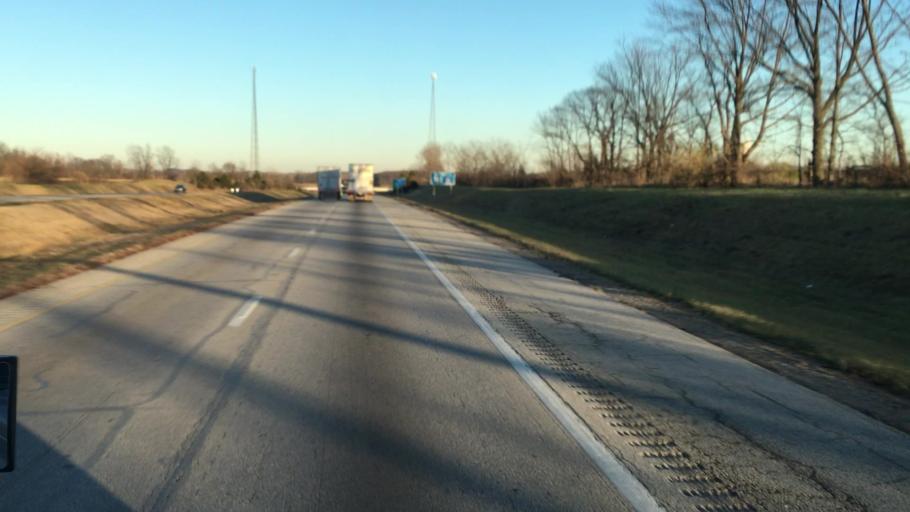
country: US
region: Ohio
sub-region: Preble County
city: Lewisburg
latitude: 39.8370
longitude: -84.5509
